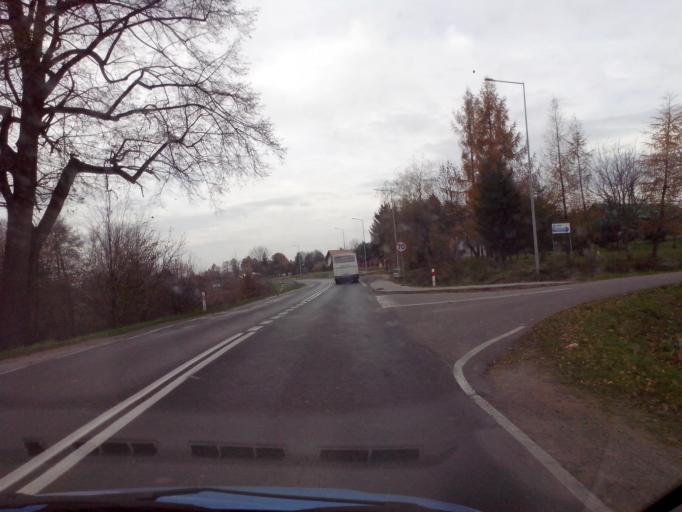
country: PL
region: Subcarpathian Voivodeship
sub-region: Powiat strzyzowski
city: Babica
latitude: 49.9338
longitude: 21.8608
